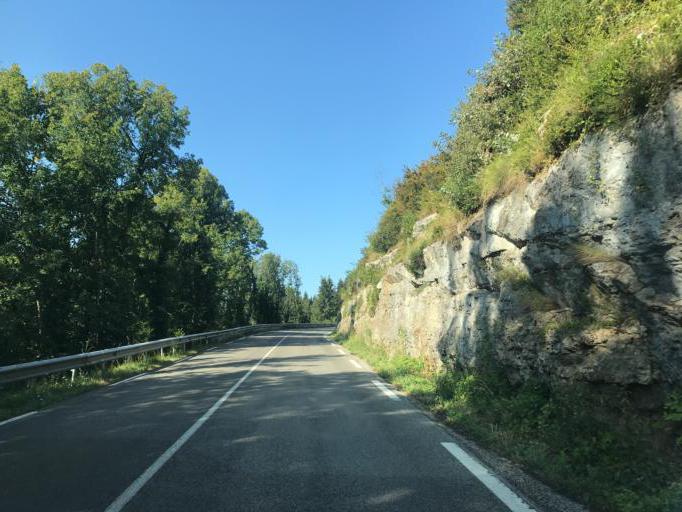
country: FR
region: Franche-Comte
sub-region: Departement du Jura
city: Lavans-les-Saint-Claude
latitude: 46.3840
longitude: 5.7736
